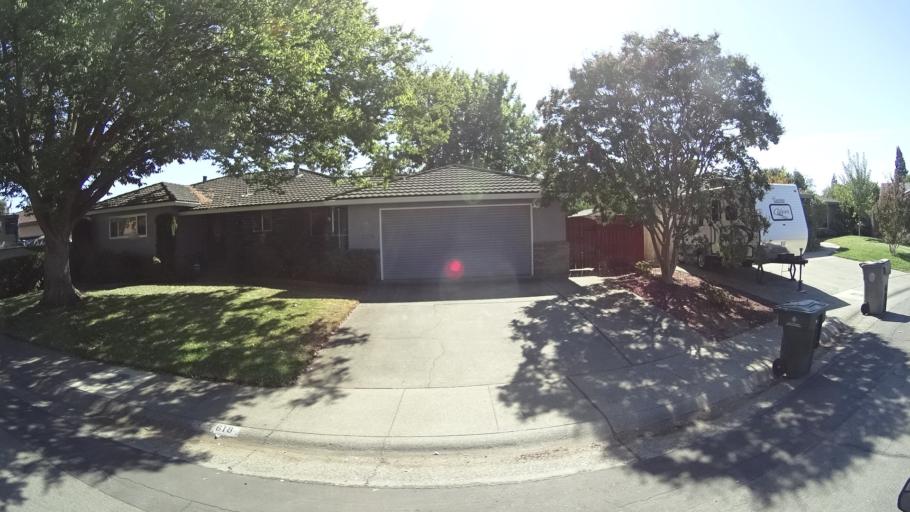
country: US
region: California
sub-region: Sacramento County
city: Parkway
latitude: 38.4808
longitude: -121.4396
